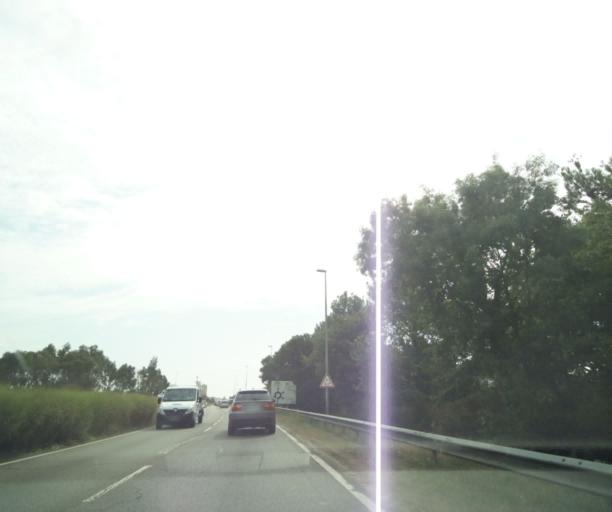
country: FR
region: Pays de la Loire
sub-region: Departement de la Loire-Atlantique
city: Saint-Herblain
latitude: 47.2113
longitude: -1.6306
